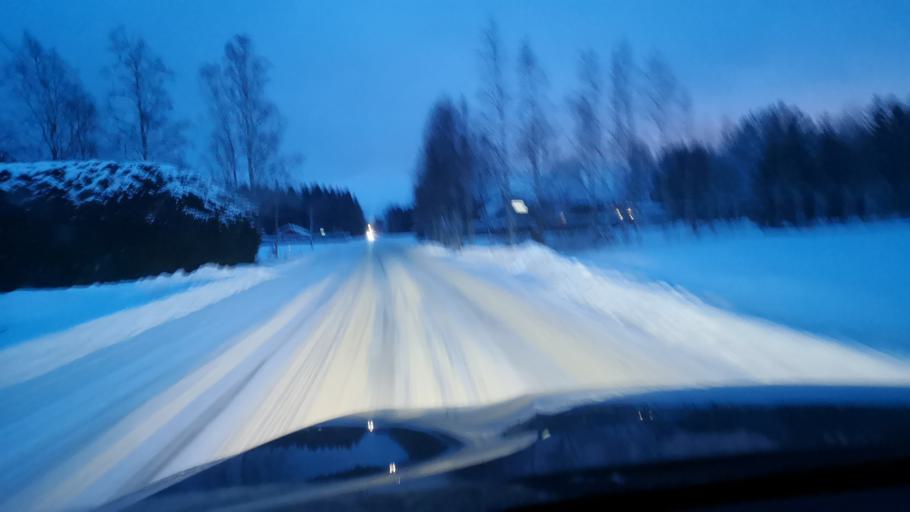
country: FI
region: Varsinais-Suomi
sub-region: Loimaa
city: Loimaa
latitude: 60.8832
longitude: 23.0891
